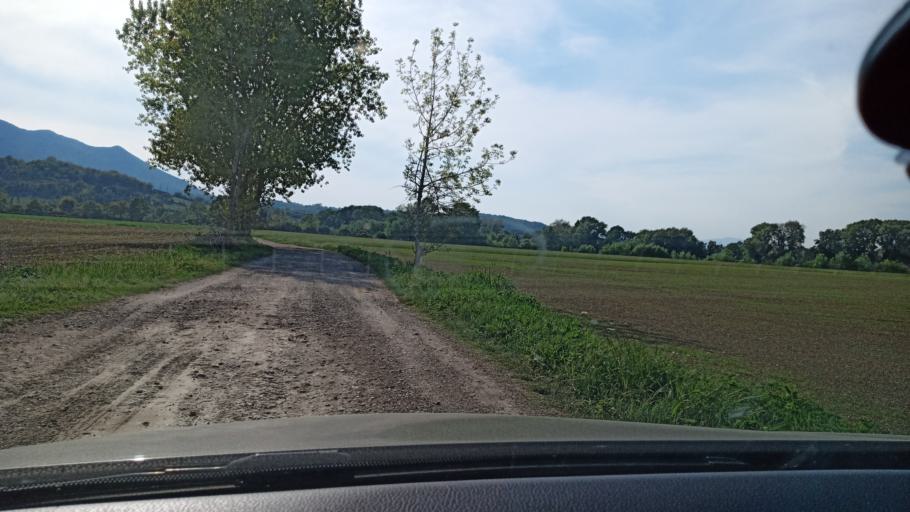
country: IT
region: Latium
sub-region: Citta metropolitana di Roma Capitale
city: Ponzano Romano
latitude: 42.2699
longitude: 12.5667
